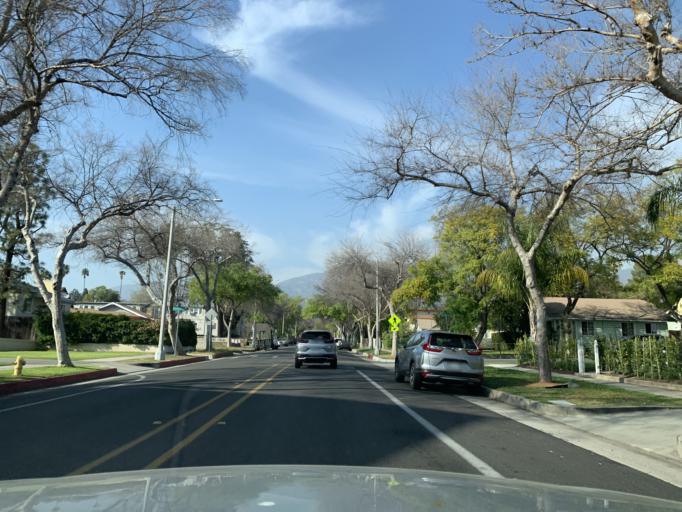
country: US
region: California
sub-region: Los Angeles County
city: Altadena
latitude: 34.1718
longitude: -118.1215
